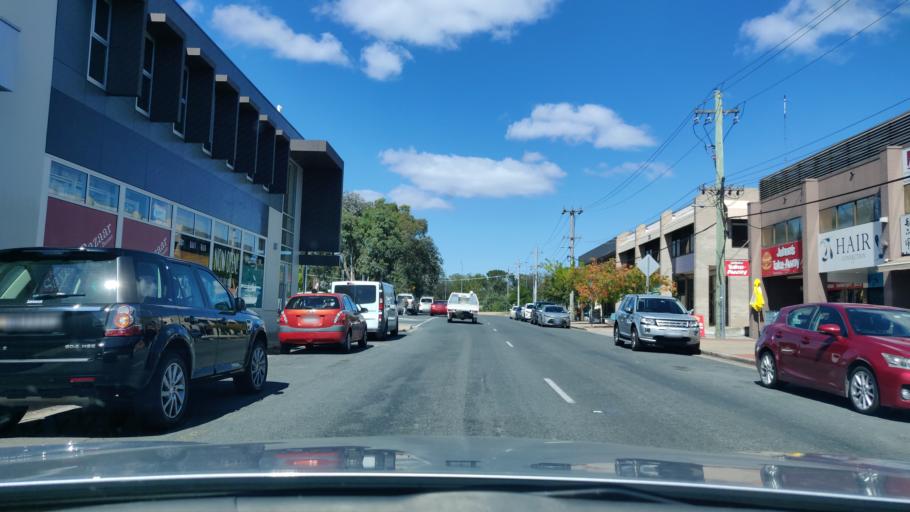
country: AU
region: Australian Capital Territory
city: Macarthur
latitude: -35.3656
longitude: 149.0939
